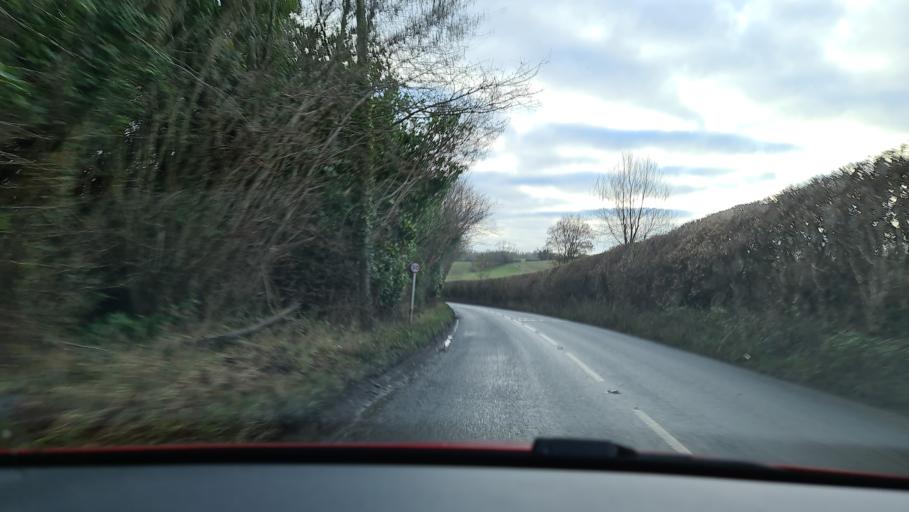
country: GB
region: England
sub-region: Buckinghamshire
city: Chesham
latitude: 51.6883
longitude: -0.5884
